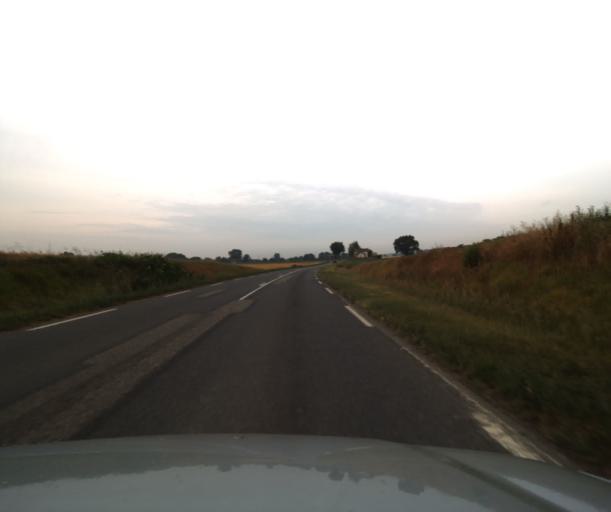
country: FR
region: Midi-Pyrenees
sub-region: Departement du Tarn-et-Garonne
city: Beaumont-de-Lomagne
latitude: 43.8307
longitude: 0.9214
